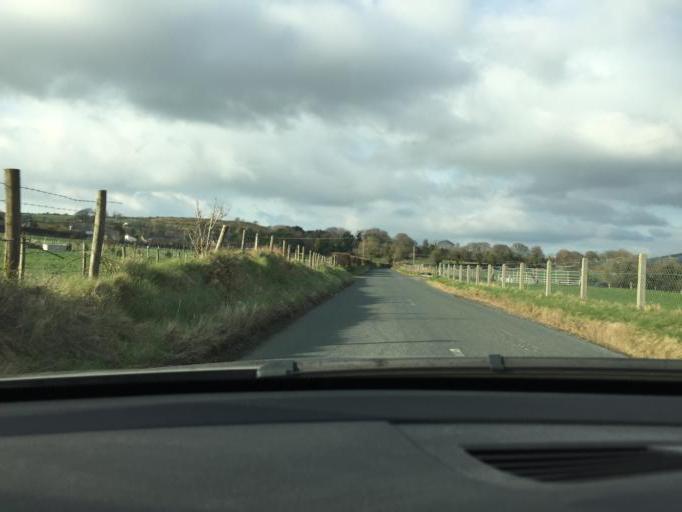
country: IE
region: Leinster
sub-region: Wicklow
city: Valleymount
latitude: 53.1256
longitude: -6.5316
